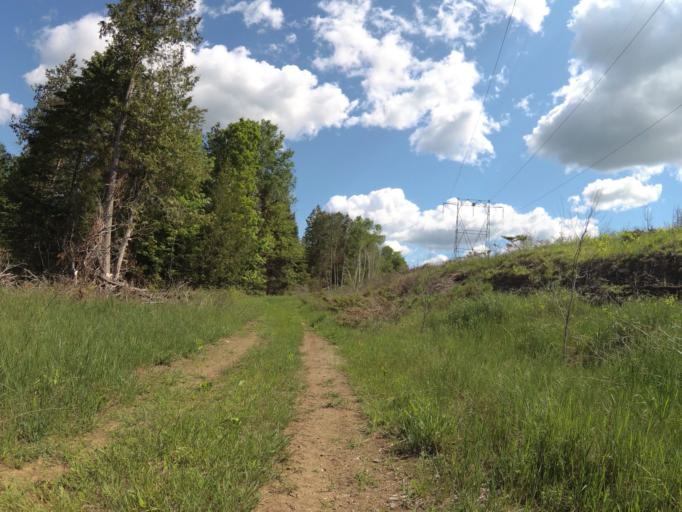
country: CA
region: Ontario
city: Renfrew
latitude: 45.0477
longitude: -76.7644
